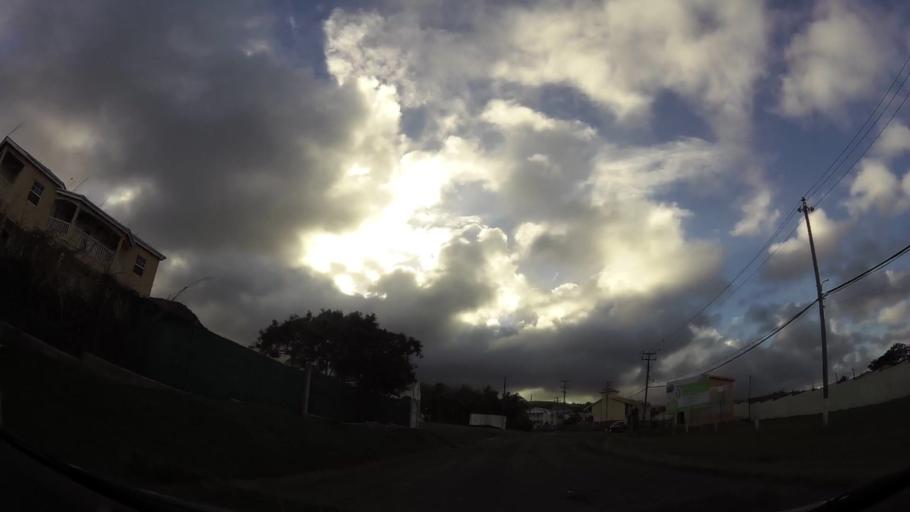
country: KN
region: Saint Mary Cayon
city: Cayon
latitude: 17.3484
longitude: -62.7276
